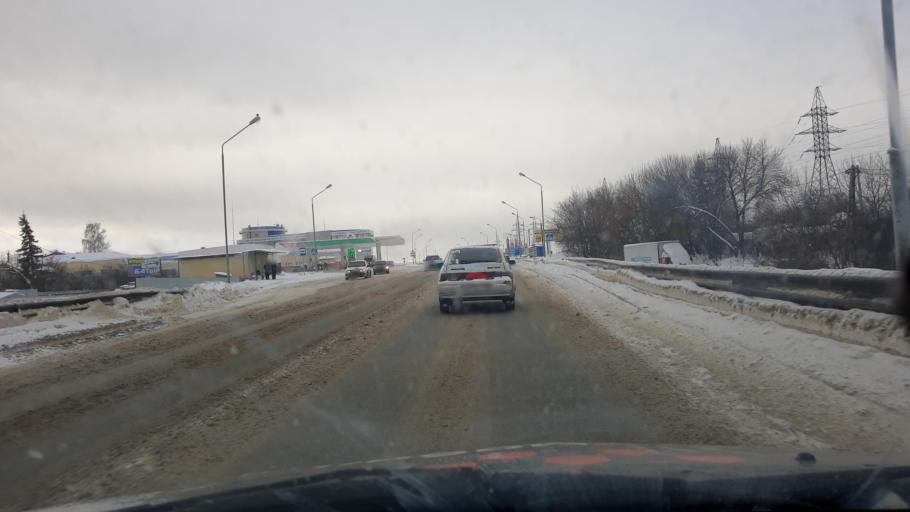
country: RU
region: Bashkortostan
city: Avdon
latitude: 54.6804
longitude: 55.8058
